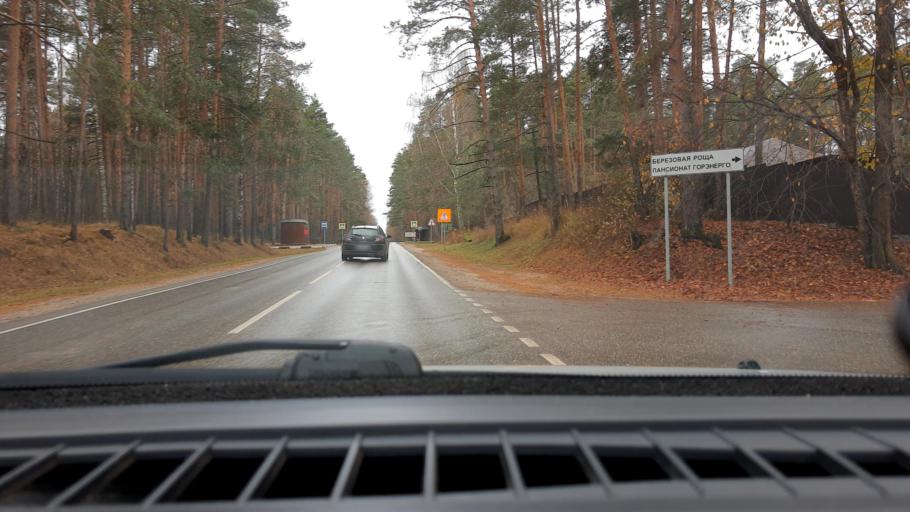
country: RU
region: Nizjnij Novgorod
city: Afonino
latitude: 56.1859
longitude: 44.1119
